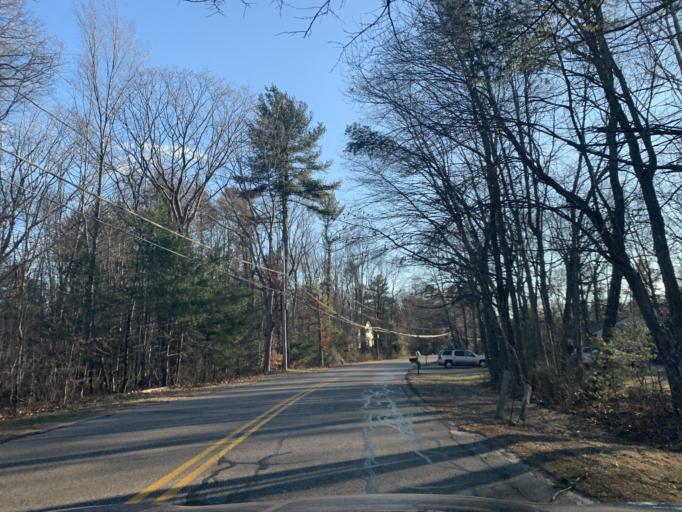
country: US
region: Massachusetts
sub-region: Bristol County
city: Norton
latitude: 41.9262
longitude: -71.1984
